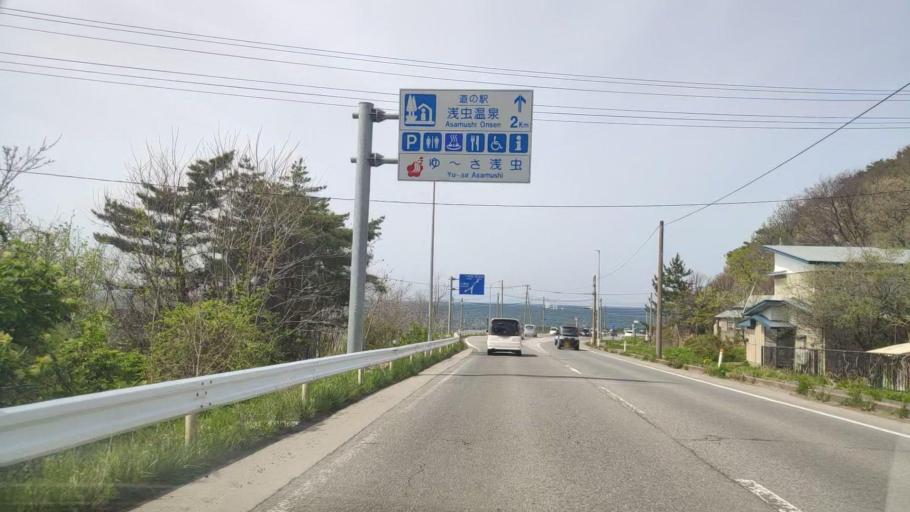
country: JP
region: Aomori
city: Aomori Shi
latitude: 40.8765
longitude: 140.8507
